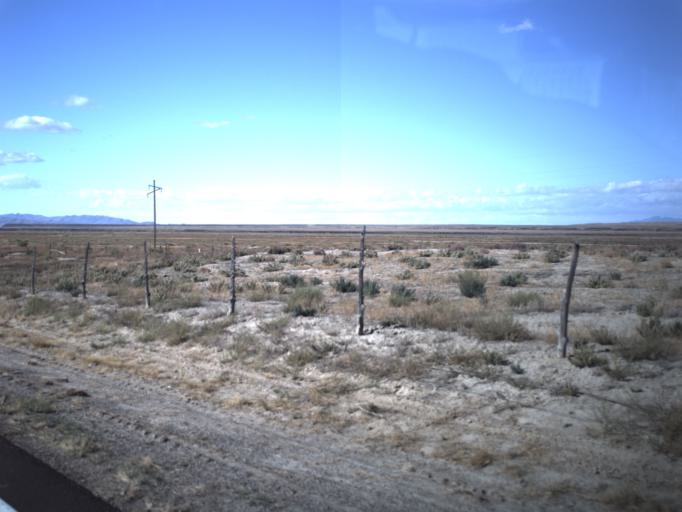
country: US
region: Utah
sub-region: Millard County
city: Delta
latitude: 39.2267
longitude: -112.6715
